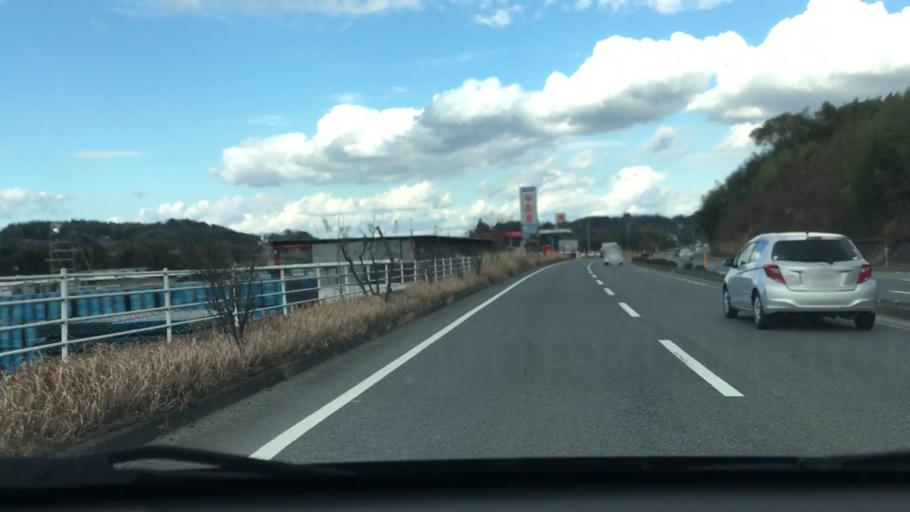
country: JP
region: Oita
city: Oita
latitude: 33.1236
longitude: 131.6545
